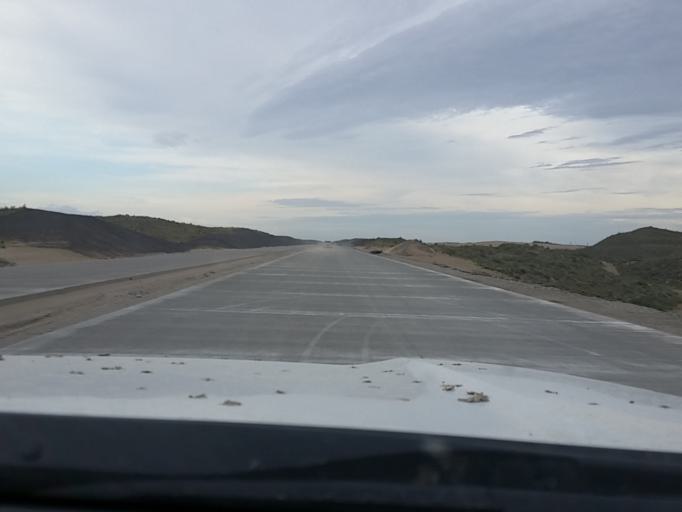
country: KZ
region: Almaty Oblysy
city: Zharkent
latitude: 44.1749
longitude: 80.2819
